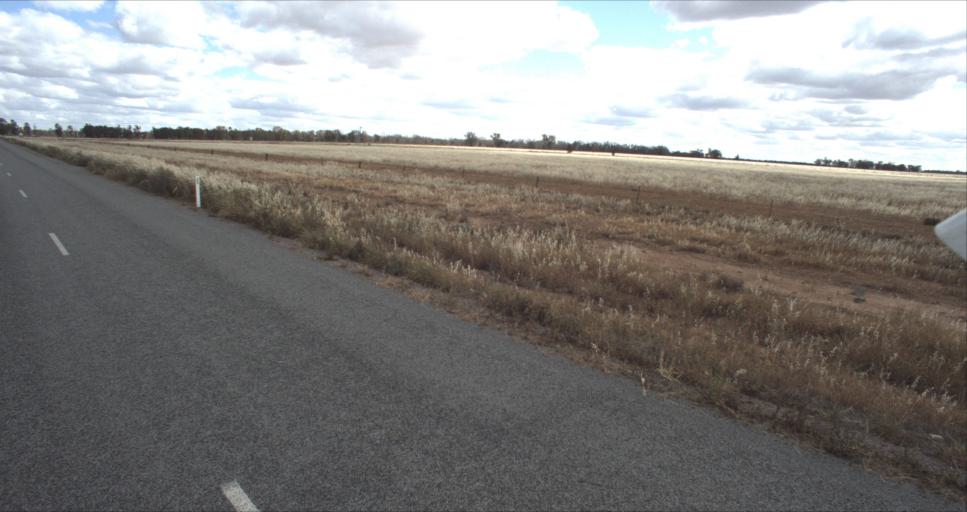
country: AU
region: New South Wales
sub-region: Leeton
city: Leeton
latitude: -34.6940
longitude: 146.3432
